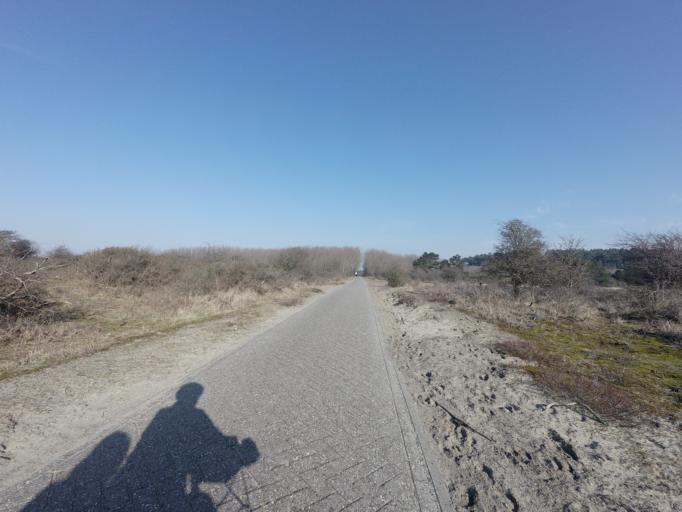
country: NL
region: North Holland
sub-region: Gemeente Bloemendaal
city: Bloemendaal
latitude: 52.4235
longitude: 4.5761
